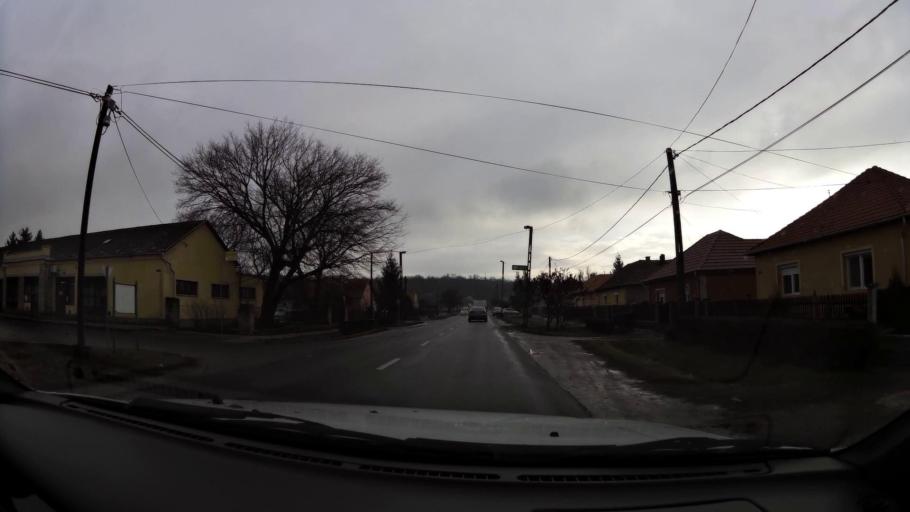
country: HU
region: Borsod-Abauj-Zemplen
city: Izsofalva
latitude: 48.2796
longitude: 20.6652
